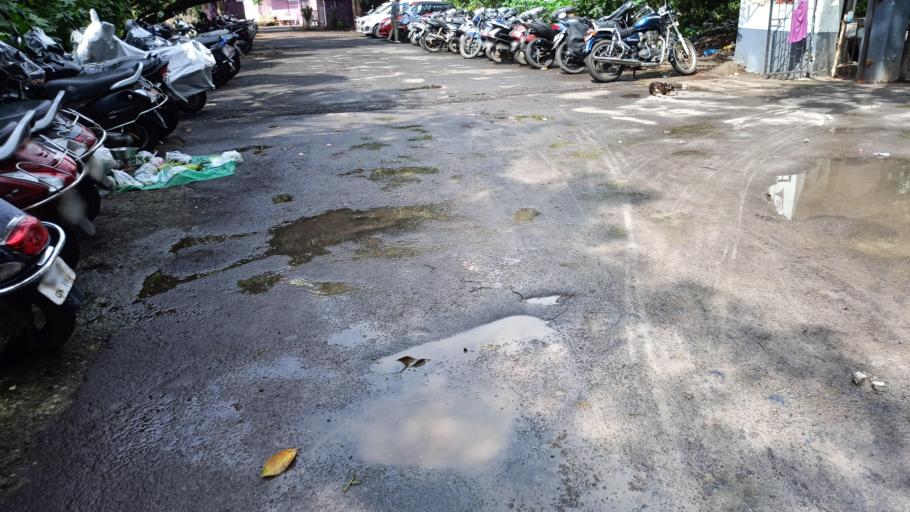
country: IN
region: Maharashtra
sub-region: Mumbai Suburban
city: Borivli
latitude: 19.2639
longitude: 72.8593
